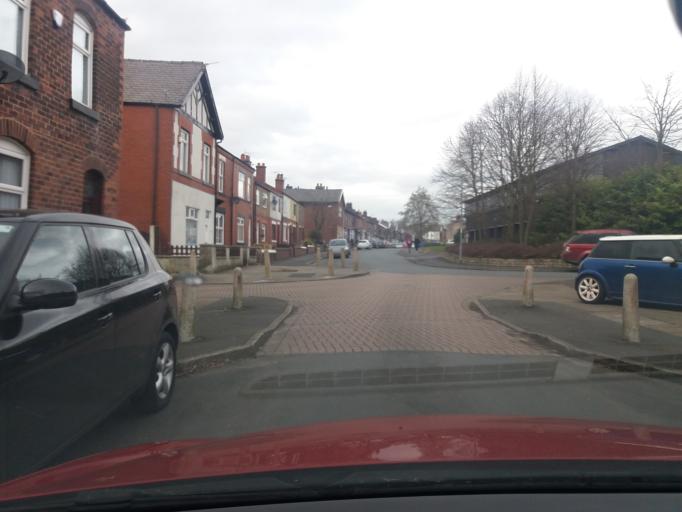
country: GB
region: England
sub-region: Lancashire
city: Chorley
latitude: 53.6589
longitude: -2.6259
